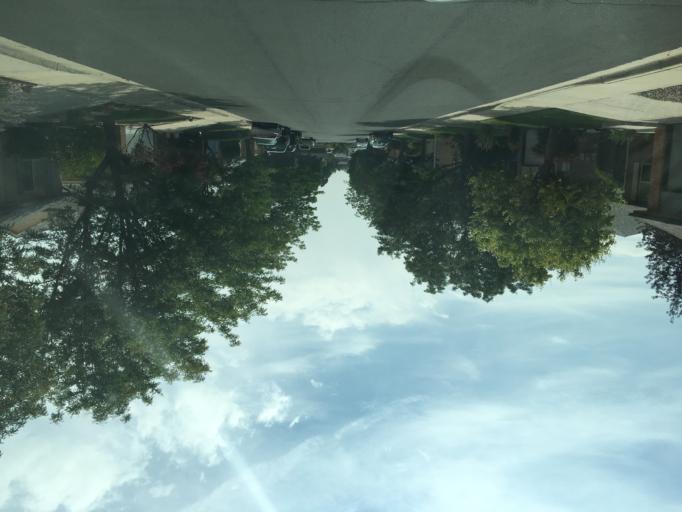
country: US
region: Colorado
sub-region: Adams County
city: Aurora
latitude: 39.7297
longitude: -104.8018
